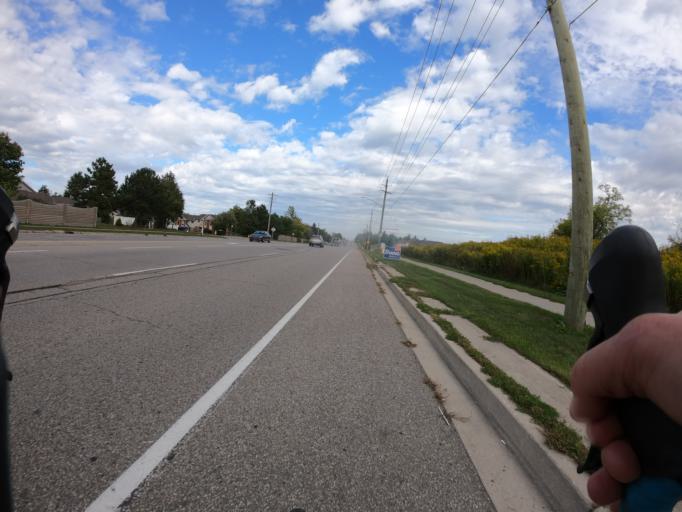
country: CA
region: Ontario
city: Waterloo
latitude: 43.4470
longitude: -80.5689
